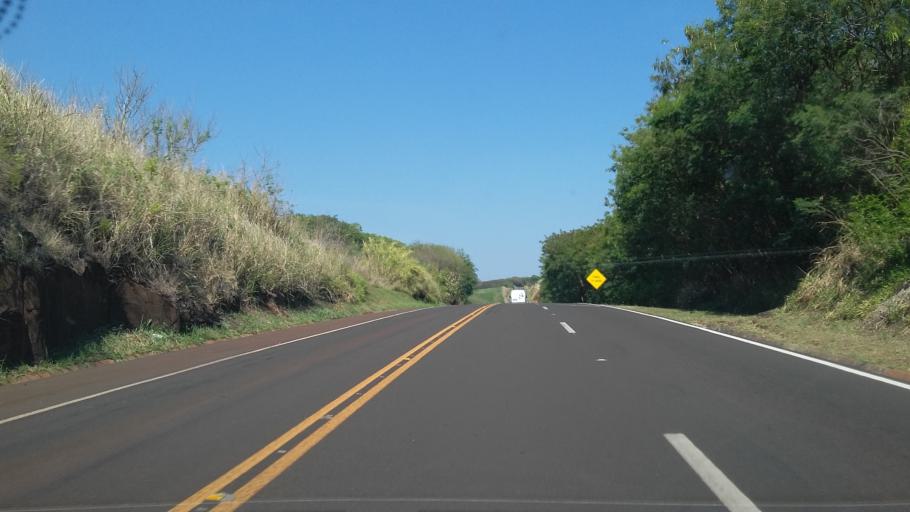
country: BR
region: Parana
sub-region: Bandeirantes
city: Bandeirantes
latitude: -23.1390
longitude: -50.3861
